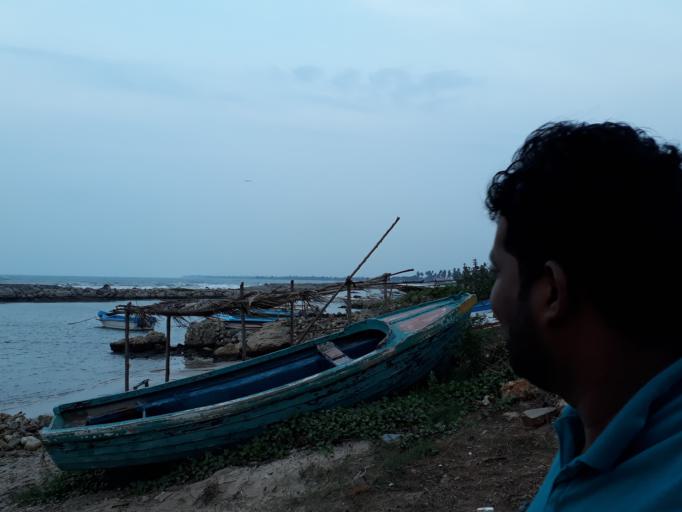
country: LK
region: Northern Province
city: Valvedditturai
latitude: 9.8094
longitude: 80.0959
